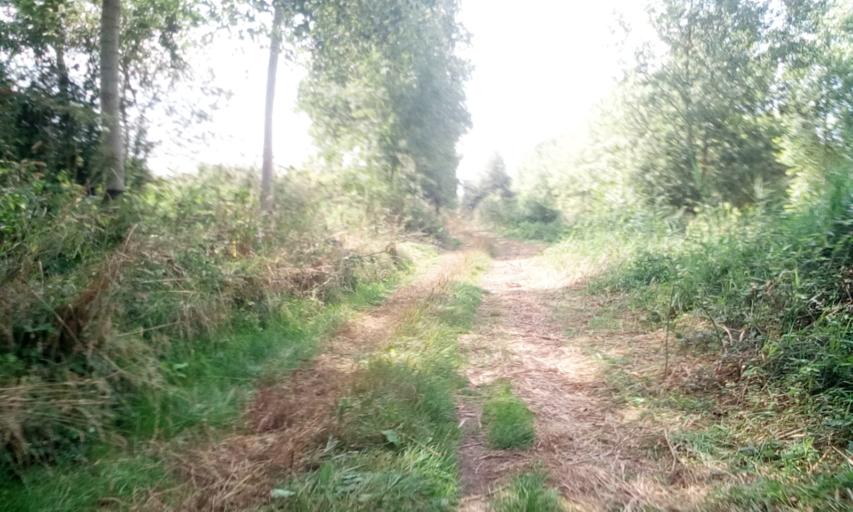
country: FR
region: Lower Normandy
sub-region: Departement du Calvados
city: Argences
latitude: 49.1492
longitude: -0.1709
